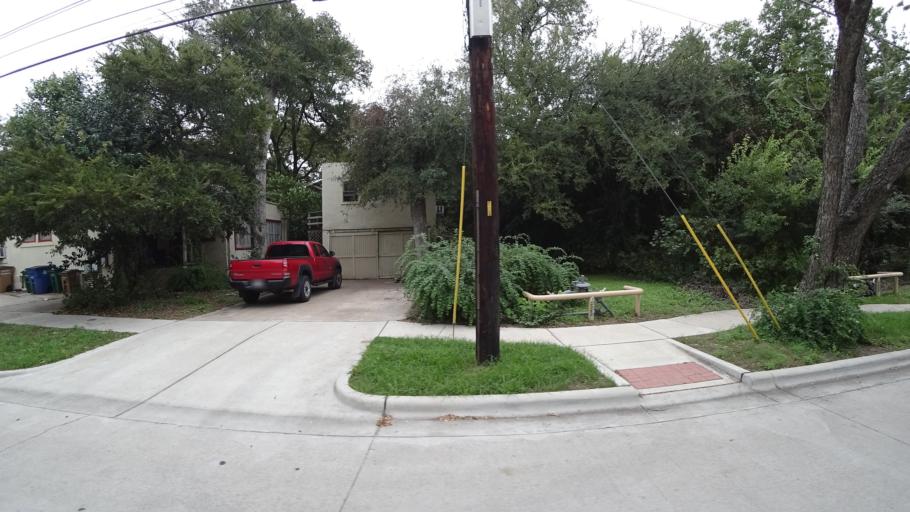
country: US
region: Texas
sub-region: Travis County
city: Austin
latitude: 30.2918
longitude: -97.7317
